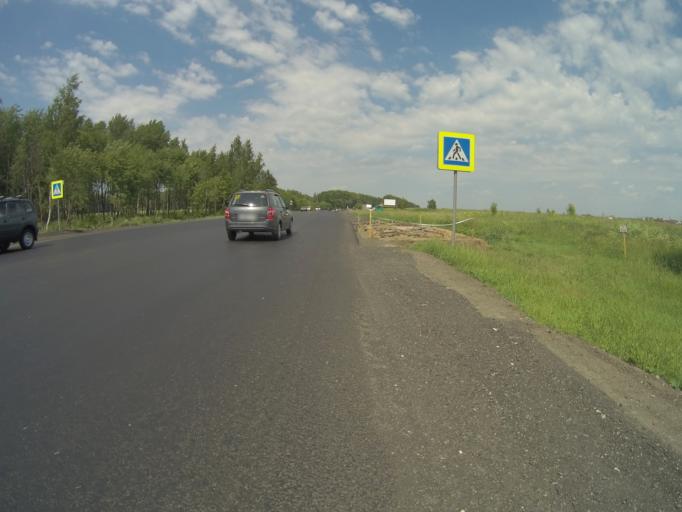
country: RU
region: Vladimir
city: Bogolyubovo
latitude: 56.2211
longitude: 40.4419
